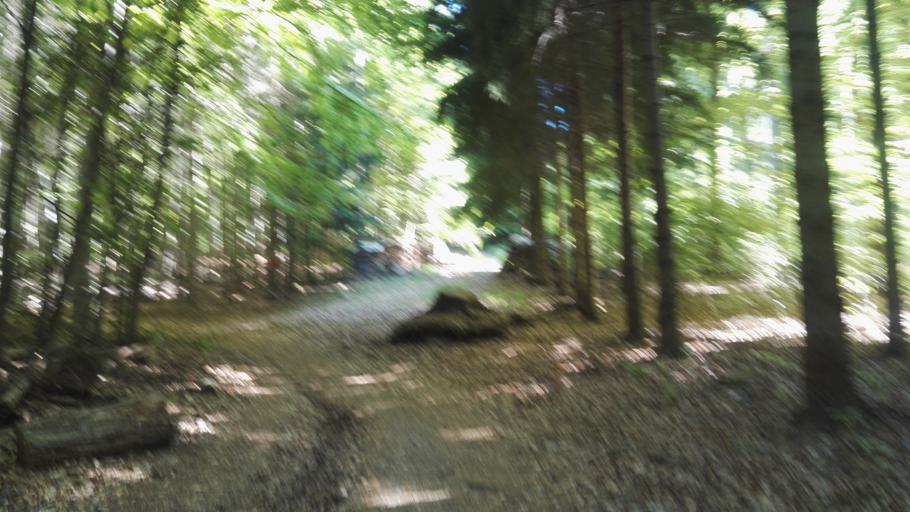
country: AT
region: Styria
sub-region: Politischer Bezirk Graz-Umgebung
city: Thal
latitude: 47.0738
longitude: 15.3703
